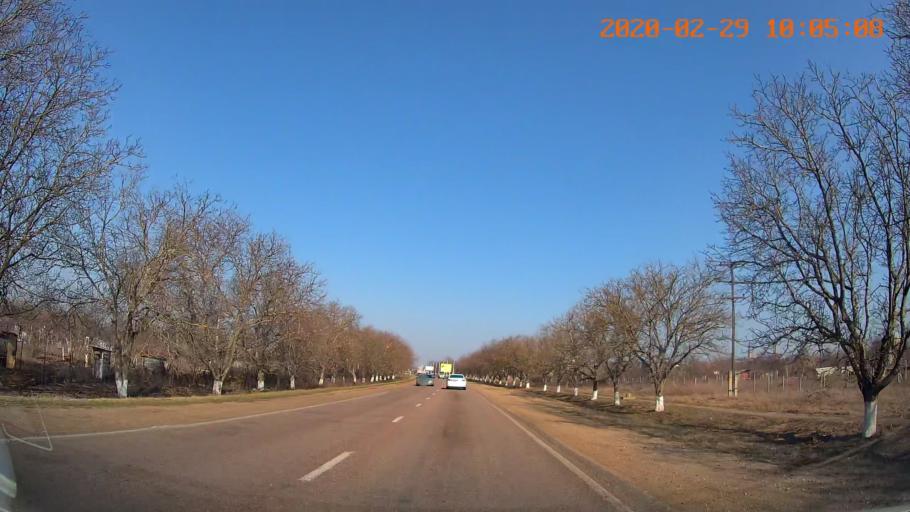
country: MD
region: Telenesti
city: Tiraspolul Nou
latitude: 46.8045
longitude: 29.6730
